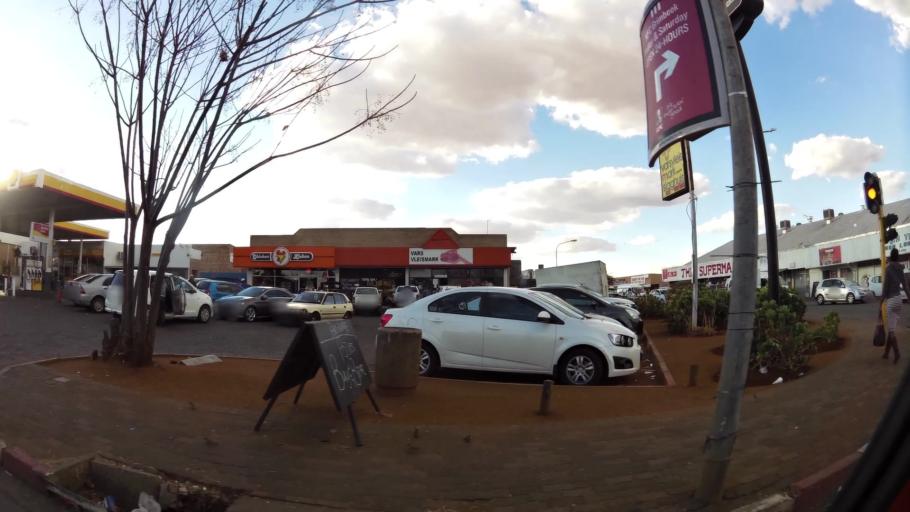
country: ZA
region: North-West
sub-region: Dr Kenneth Kaunda District Municipality
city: Potchefstroom
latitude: -26.7146
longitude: 27.1009
